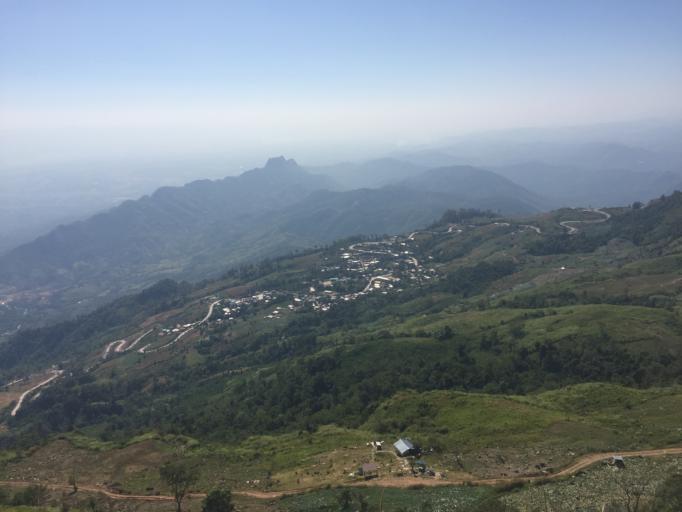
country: TH
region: Phetchabun
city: Lom Kao
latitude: 16.8966
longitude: 101.1066
